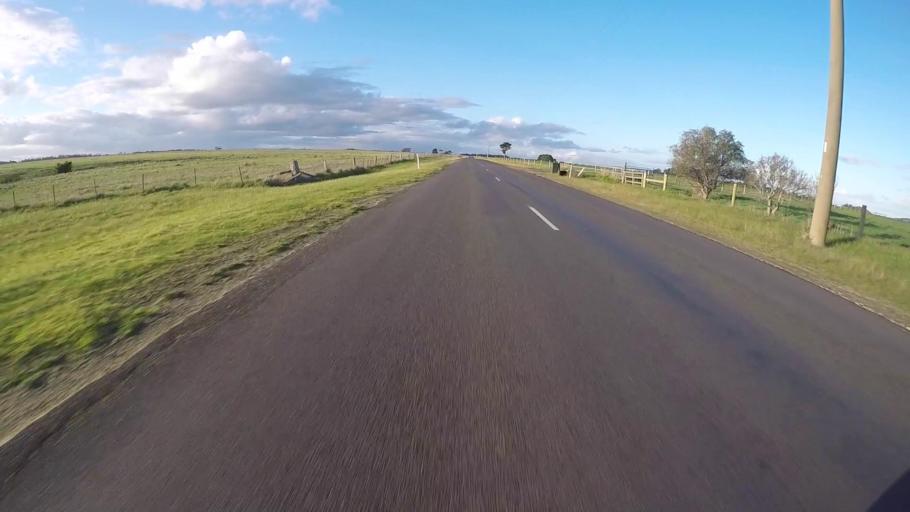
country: AU
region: Victoria
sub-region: Greater Geelong
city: Wandana Heights
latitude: -38.1414
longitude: 144.1940
